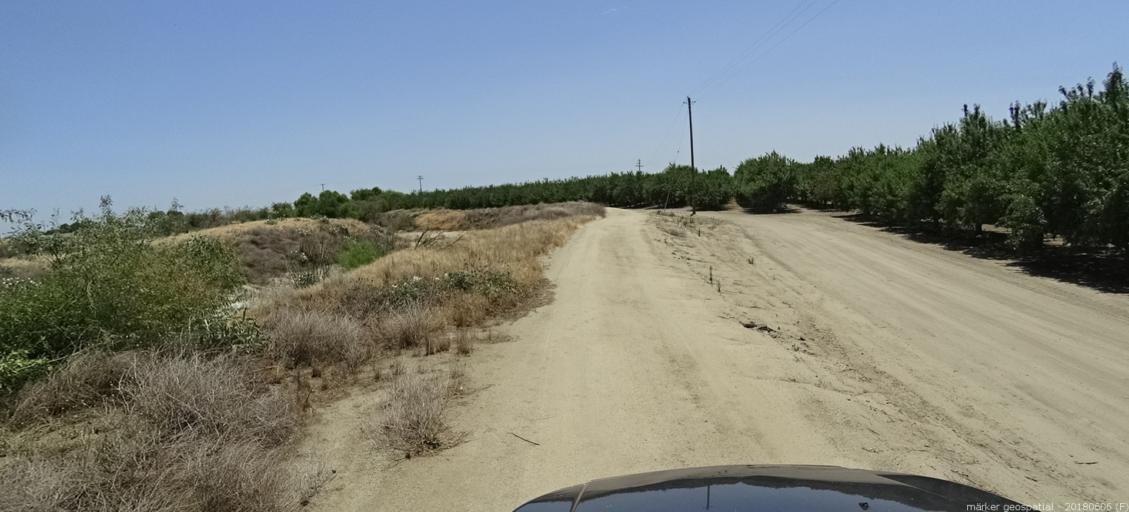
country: US
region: California
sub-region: Fresno County
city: Mendota
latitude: 36.7772
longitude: -120.2895
